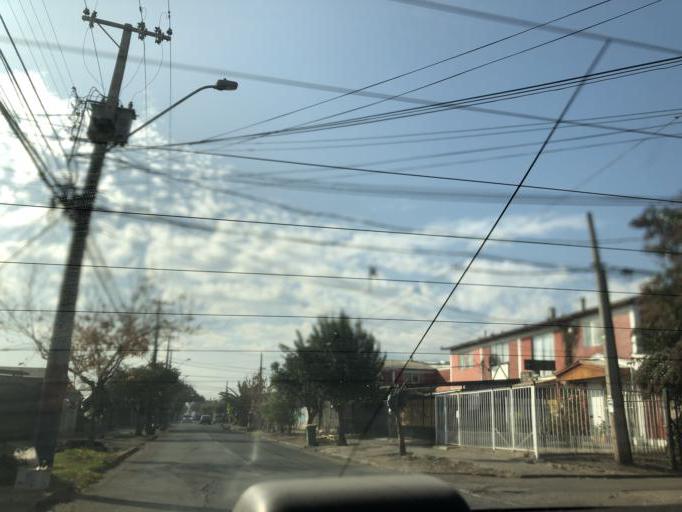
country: CL
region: Santiago Metropolitan
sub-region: Provincia de Cordillera
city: Puente Alto
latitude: -33.5916
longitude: -70.5730
